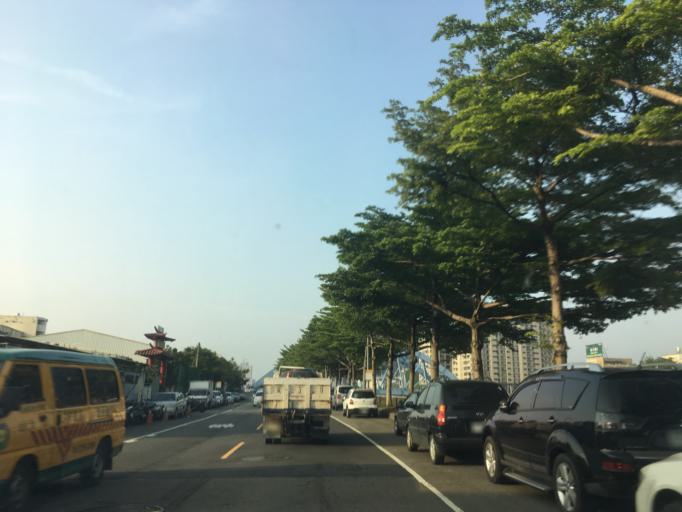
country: TW
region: Taiwan
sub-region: Taichung City
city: Taichung
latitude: 24.1571
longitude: 120.7037
